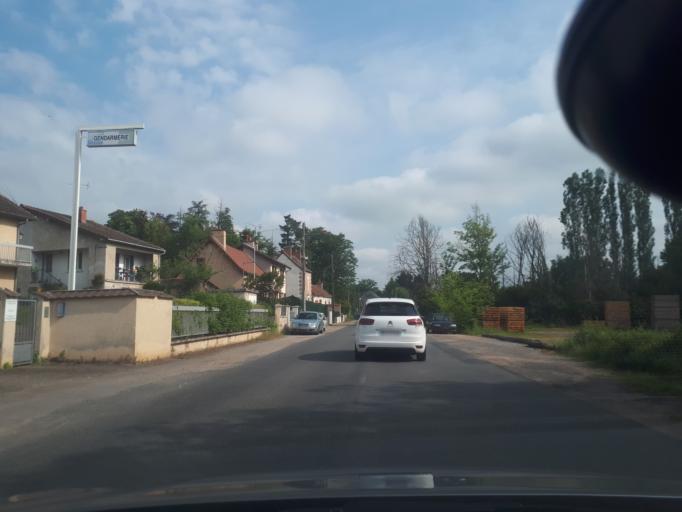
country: FR
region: Auvergne
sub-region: Departement de l'Allier
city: Saint-Gerand-le-Puy
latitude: 46.3807
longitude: 3.5831
